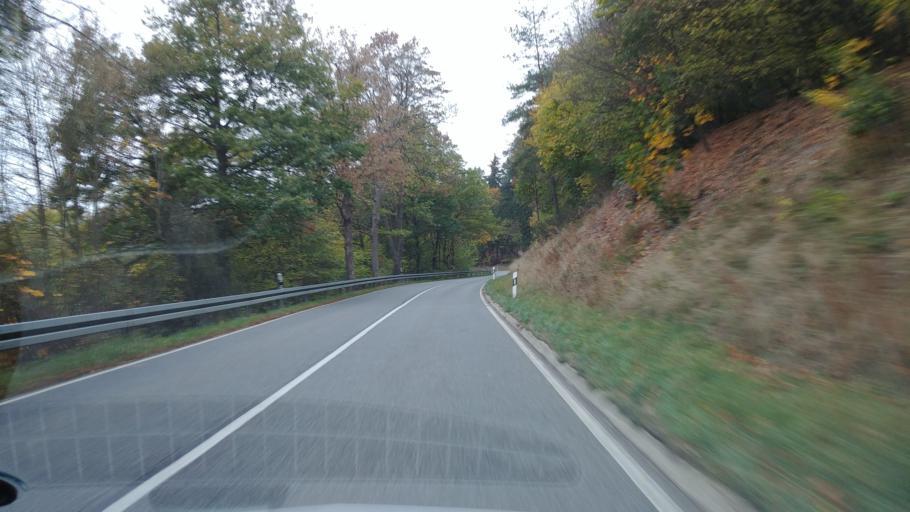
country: DE
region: Hesse
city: Taunusstein
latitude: 50.1582
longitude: 8.1555
